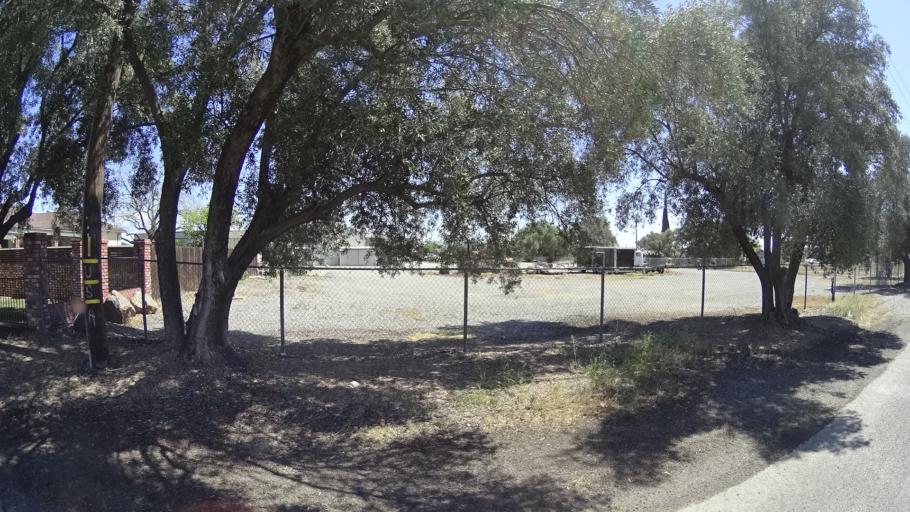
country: US
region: California
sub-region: Glenn County
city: Orland
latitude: 39.7450
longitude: -122.1781
